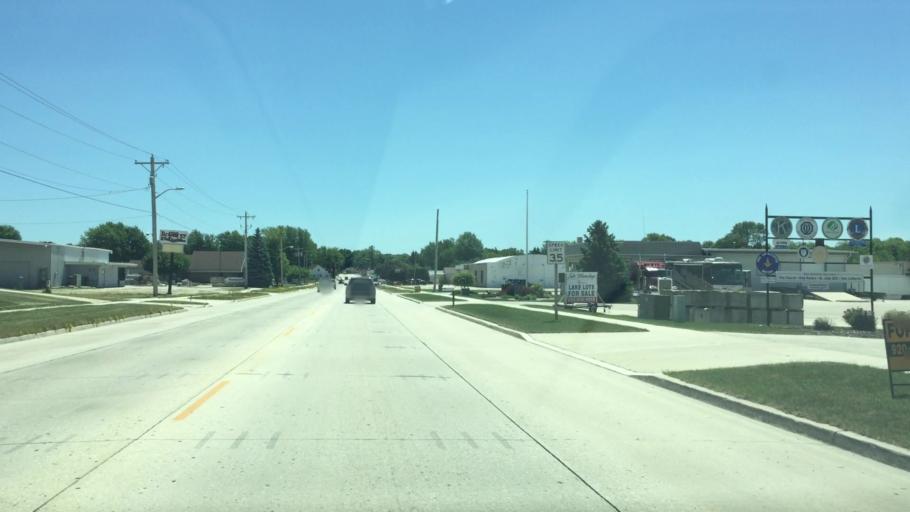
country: US
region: Wisconsin
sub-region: Calumet County
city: New Holstein
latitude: 43.9548
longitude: -88.1054
